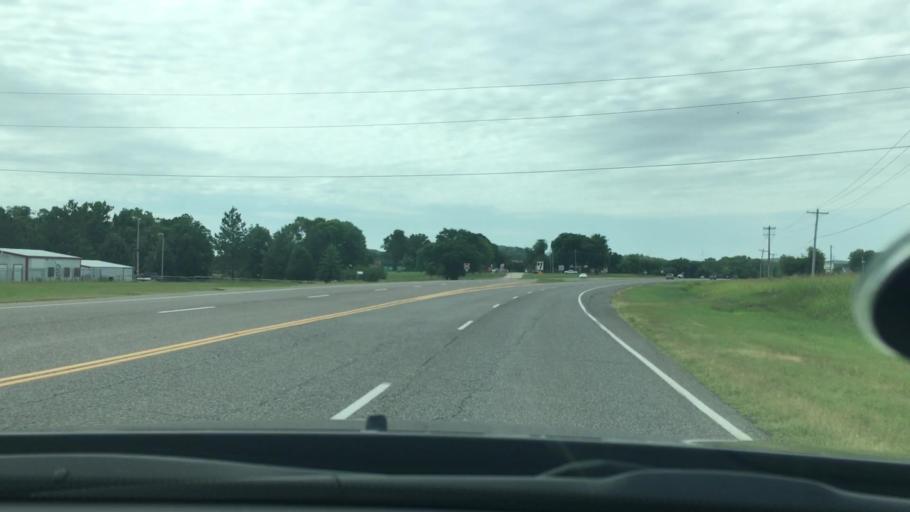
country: US
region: Oklahoma
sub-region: Murray County
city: Davis
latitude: 34.4647
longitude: -97.1307
